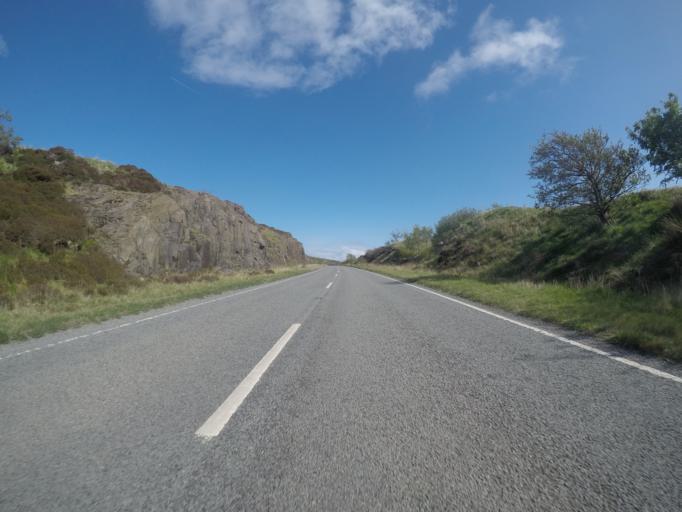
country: GB
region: Scotland
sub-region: Highland
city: Portree
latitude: 57.6154
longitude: -6.1867
